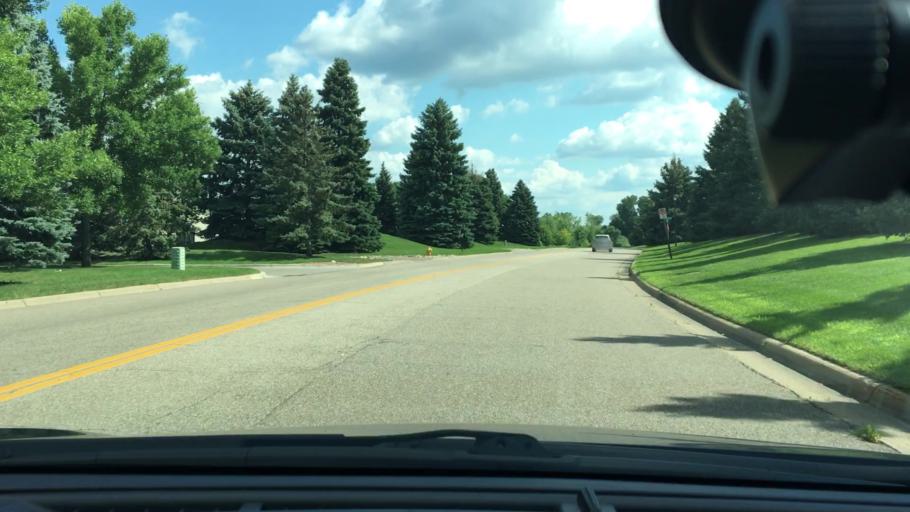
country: US
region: Minnesota
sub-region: Hennepin County
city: New Hope
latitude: 45.0530
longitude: -93.4057
